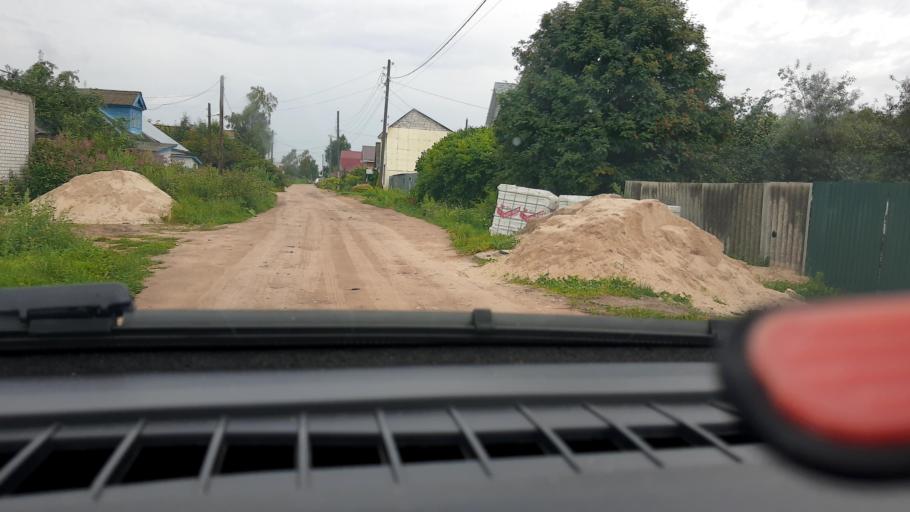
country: RU
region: Nizjnij Novgorod
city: Bor
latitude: 56.3527
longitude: 44.1303
